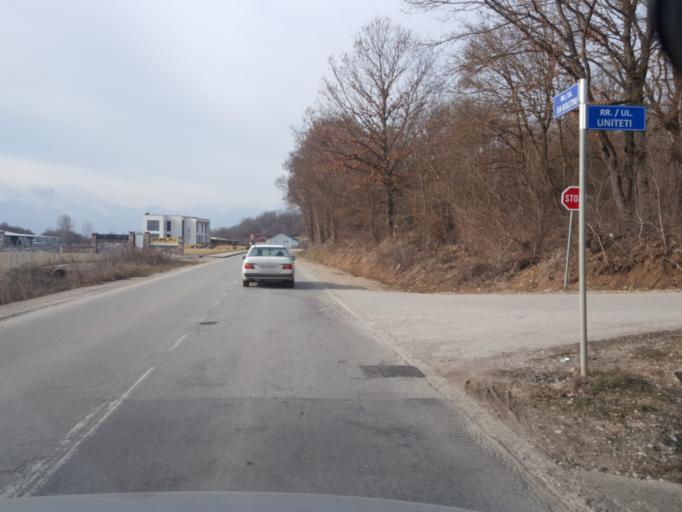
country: XK
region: Pec
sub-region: Komuna e Istogut
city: Istok
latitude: 42.6906
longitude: 20.5044
